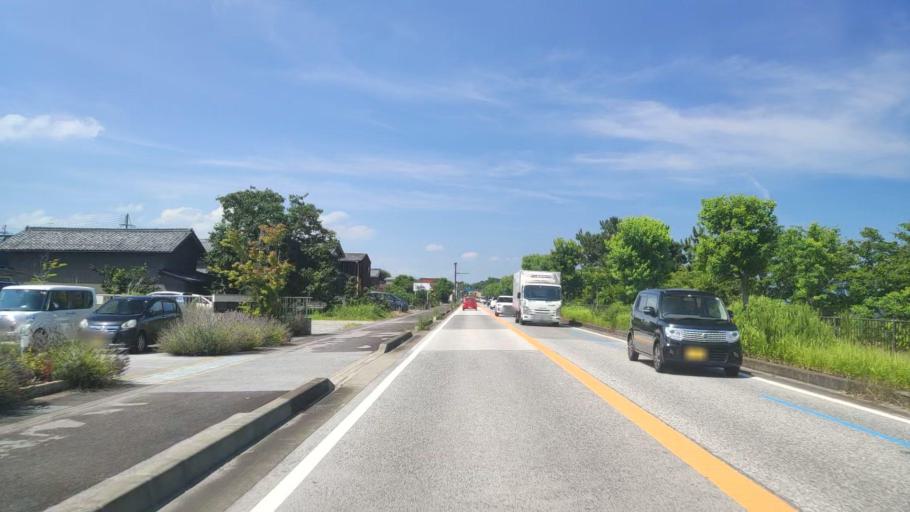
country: JP
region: Shiga Prefecture
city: Hikone
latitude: 35.2719
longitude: 136.2306
